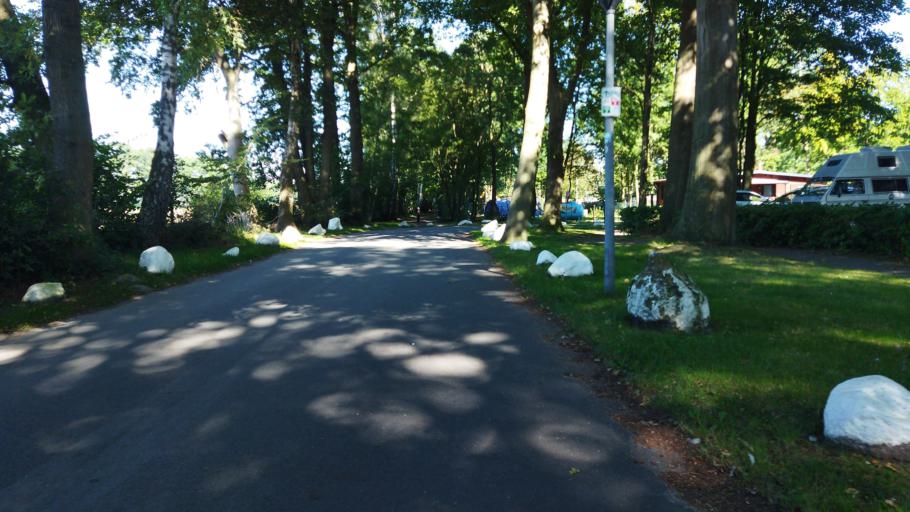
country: DE
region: Lower Saxony
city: Ostercappeln
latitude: 52.3713
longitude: 8.2294
